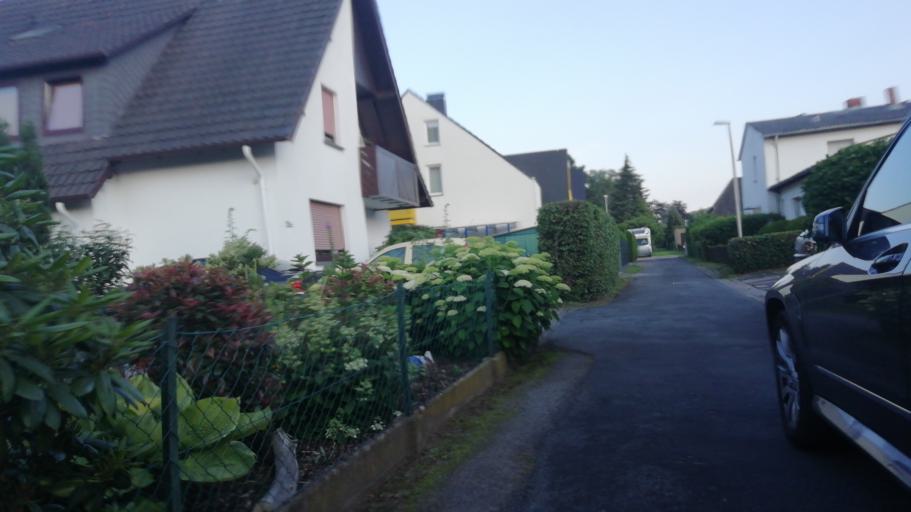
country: DE
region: North Rhine-Westphalia
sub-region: Regierungsbezirk Detmold
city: Minden
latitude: 52.2749
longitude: 8.8959
